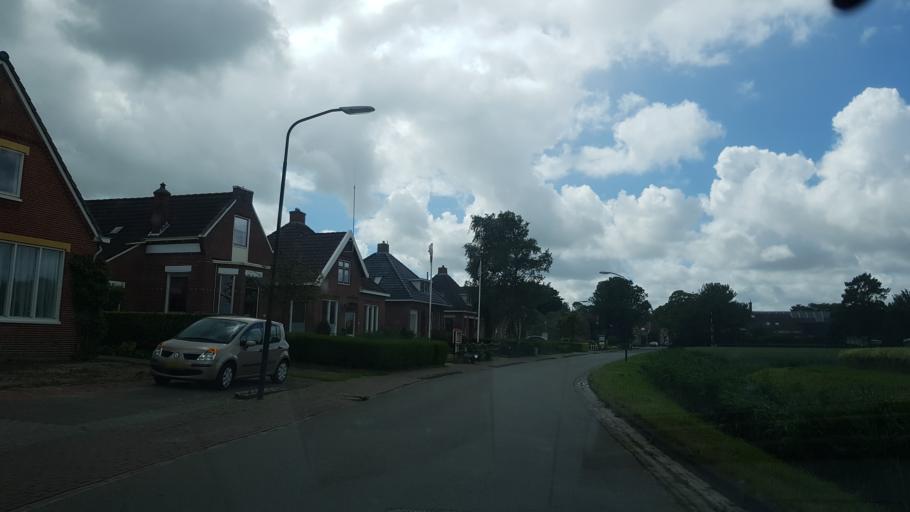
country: NL
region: Groningen
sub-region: Gemeente Winsum
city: Winsum
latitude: 53.3997
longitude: 6.4577
